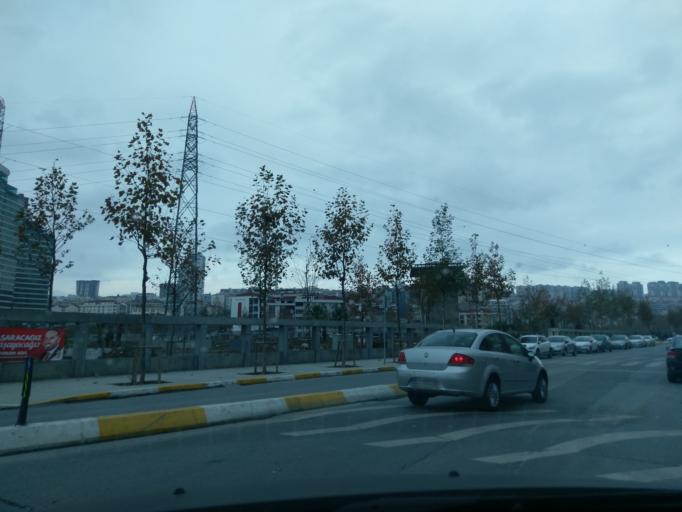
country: TR
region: Istanbul
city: Esenyurt
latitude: 41.0129
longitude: 28.6778
